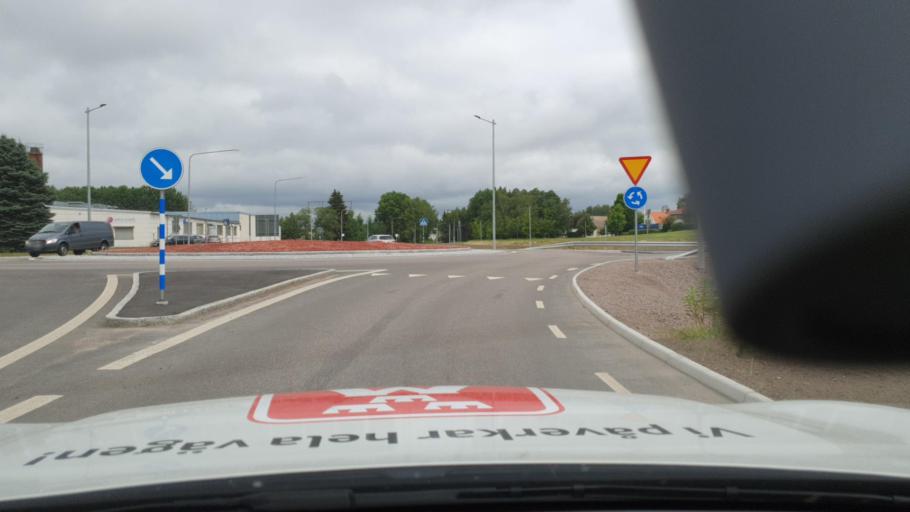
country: SE
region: Vaestra Goetaland
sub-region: Tibro Kommun
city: Tibro
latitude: 58.4134
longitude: 14.1541
